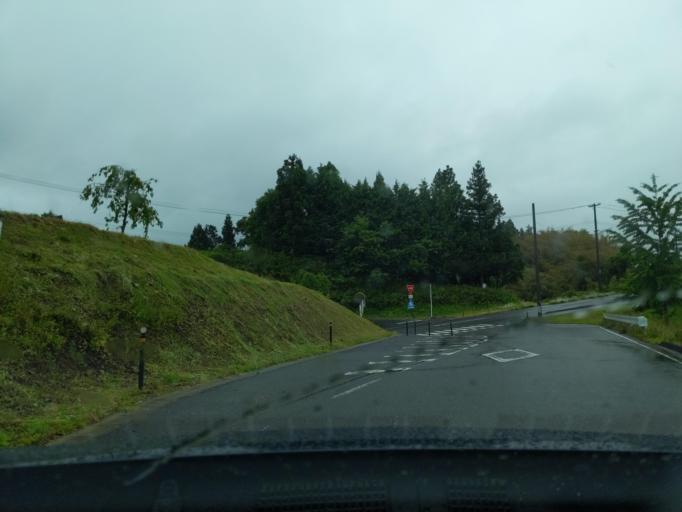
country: JP
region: Fukushima
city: Nihommatsu
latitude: 37.5918
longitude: 140.5729
